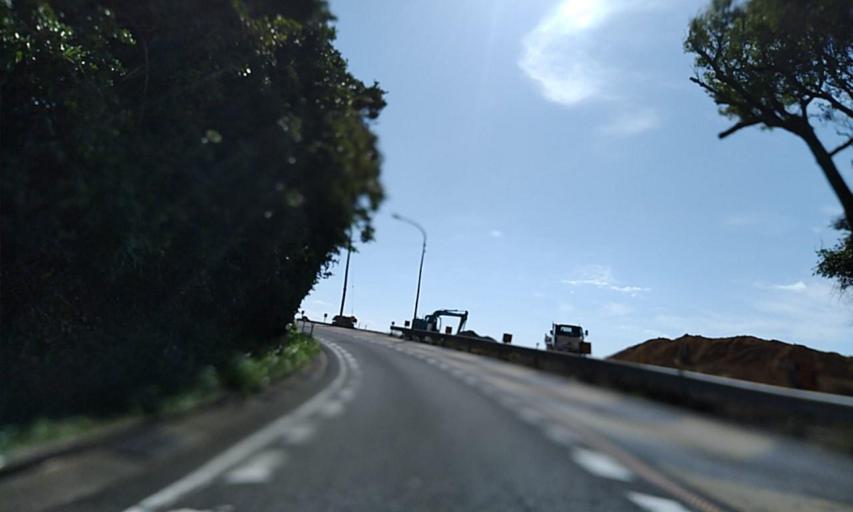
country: JP
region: Wakayama
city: Gobo
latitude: 33.7852
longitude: 135.2339
